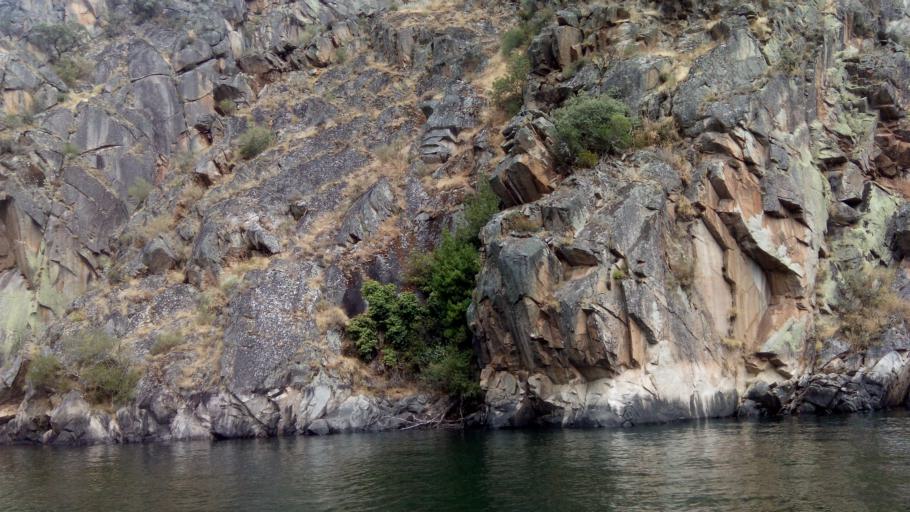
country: ES
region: Galicia
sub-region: Provincia de Lugo
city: Lobios
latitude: 42.3902
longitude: -7.5531
